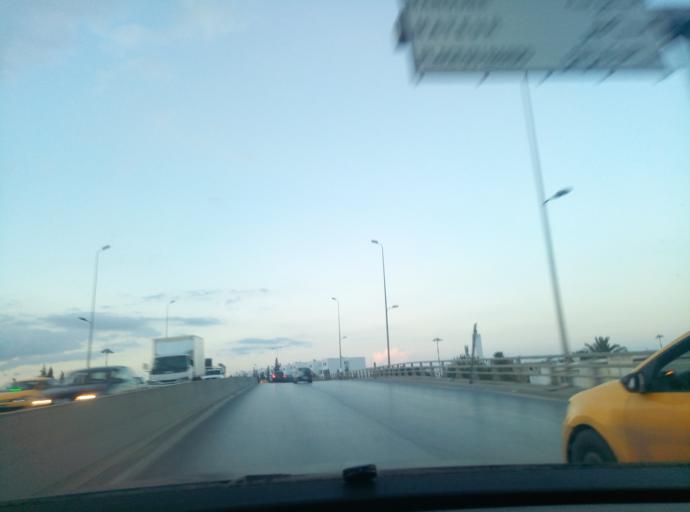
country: TN
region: Manouba
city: Manouba
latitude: 36.8099
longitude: 10.1195
